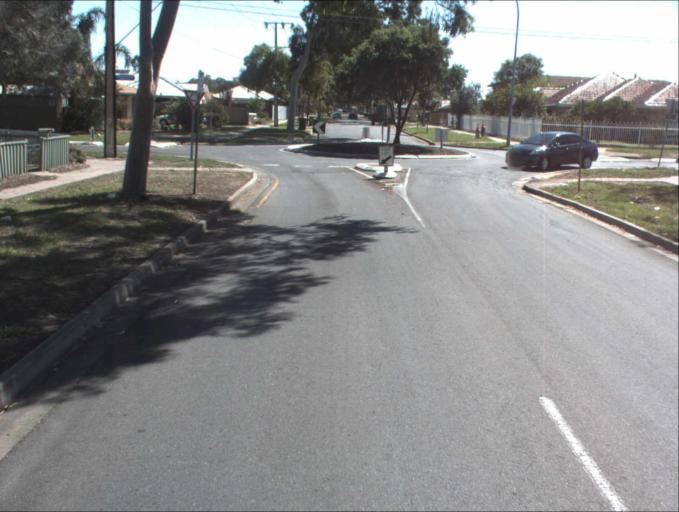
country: AU
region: South Australia
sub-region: Port Adelaide Enfield
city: Klemzig
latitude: -34.8697
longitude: 138.6339
